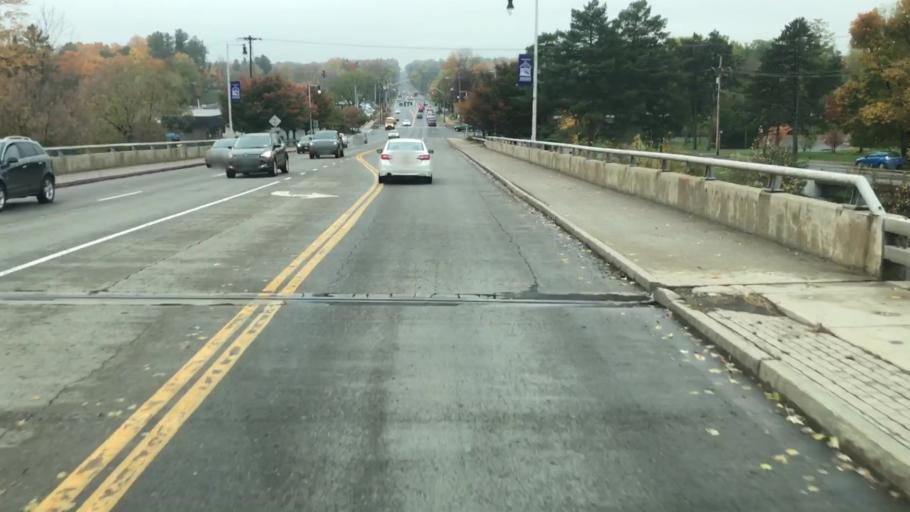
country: US
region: New York
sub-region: Onondaga County
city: Fayetteville
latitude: 43.0294
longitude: -76.0124
